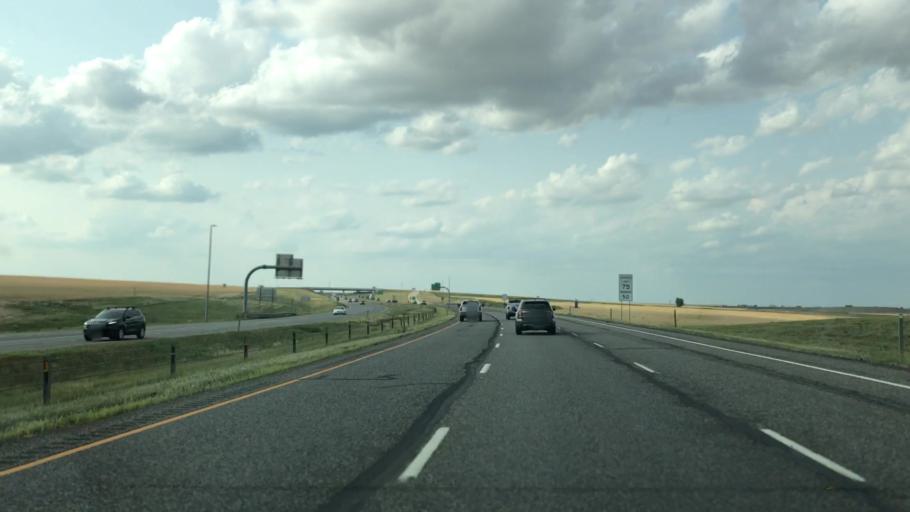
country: US
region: Colorado
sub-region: Adams County
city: Aurora
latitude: 39.8044
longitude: -104.7163
